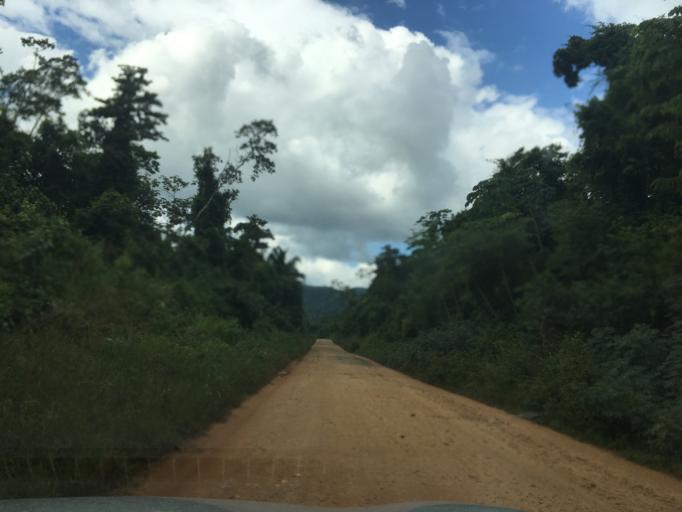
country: BZ
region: Stann Creek
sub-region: Dangriga
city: Dangriga
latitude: 16.9376
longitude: -88.3657
